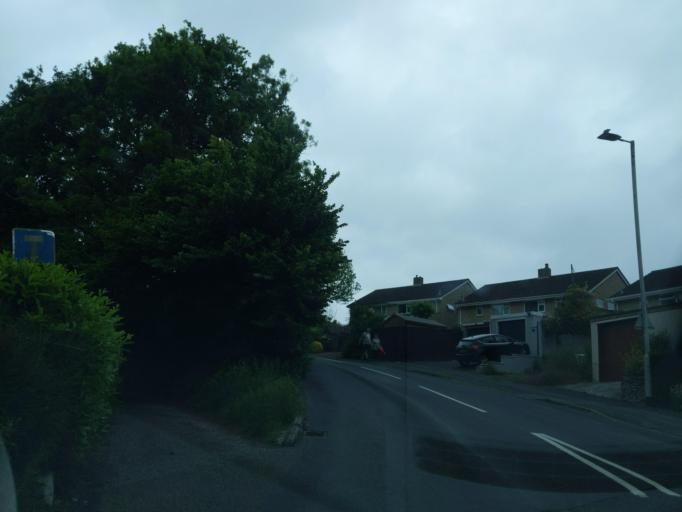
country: GB
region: England
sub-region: Devon
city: Plympton
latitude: 50.3803
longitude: -4.0386
